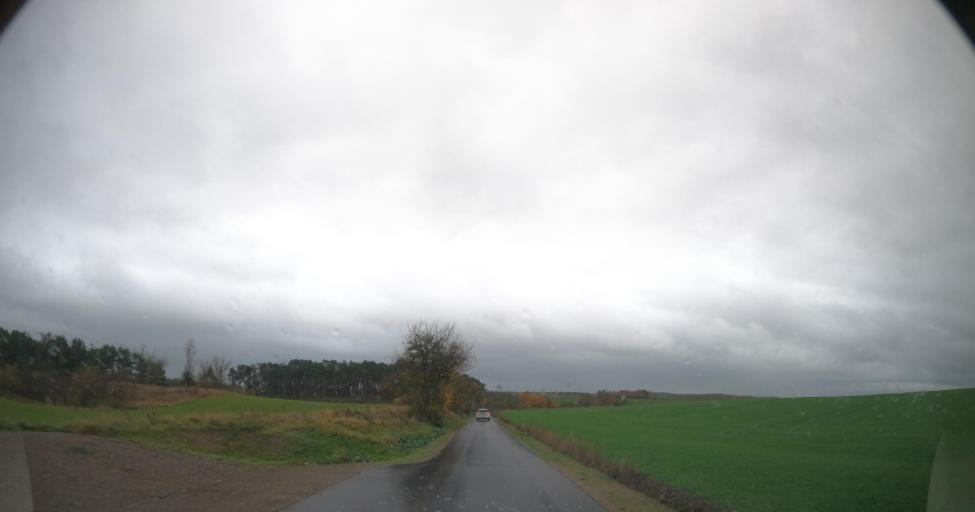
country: PL
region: West Pomeranian Voivodeship
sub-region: Powiat policki
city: Kolbaskowo
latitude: 53.3656
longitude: 14.3678
